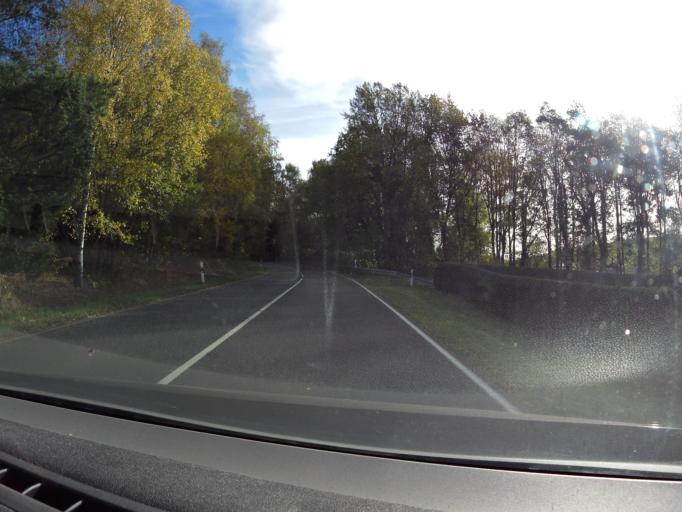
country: DE
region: Thuringia
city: Martinroda
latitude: 50.6972
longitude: 10.8940
